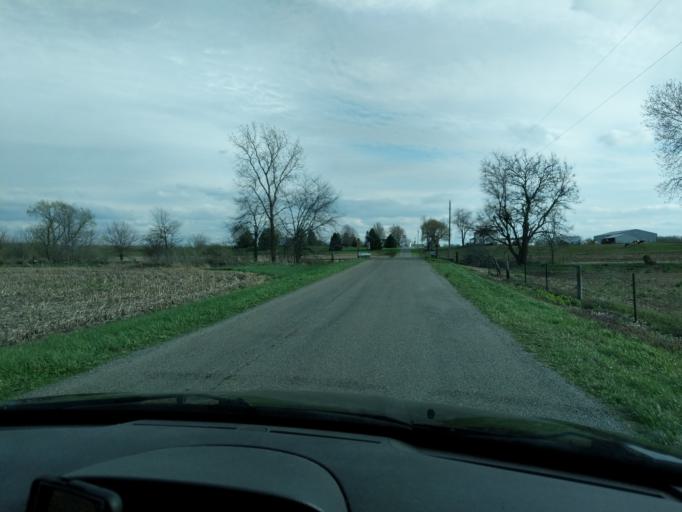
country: US
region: Ohio
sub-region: Logan County
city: West Liberty
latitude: 40.2040
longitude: -83.6879
